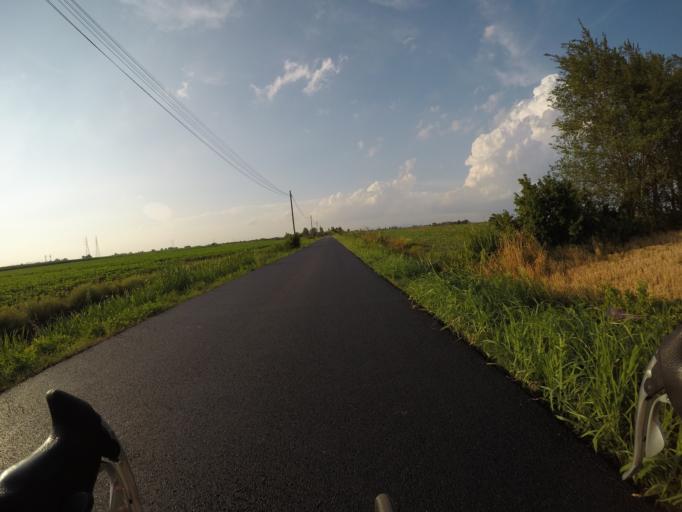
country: IT
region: Veneto
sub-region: Provincia di Rovigo
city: San Bellino
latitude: 45.0323
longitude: 11.5857
